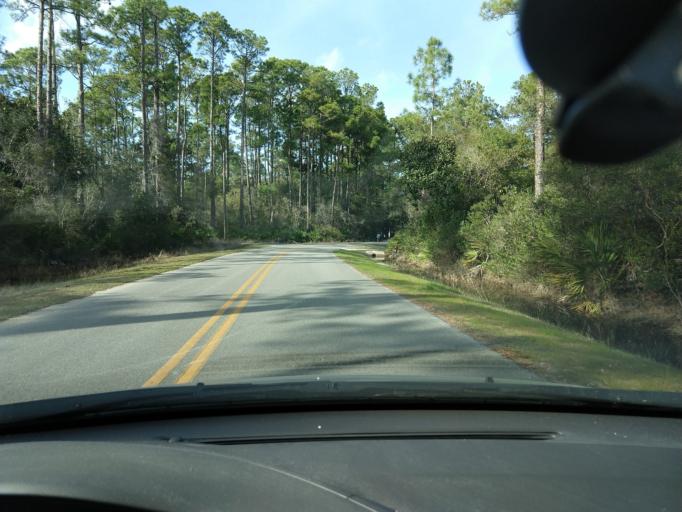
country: US
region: Florida
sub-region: Walton County
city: Seaside
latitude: 30.3765
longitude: -86.1245
